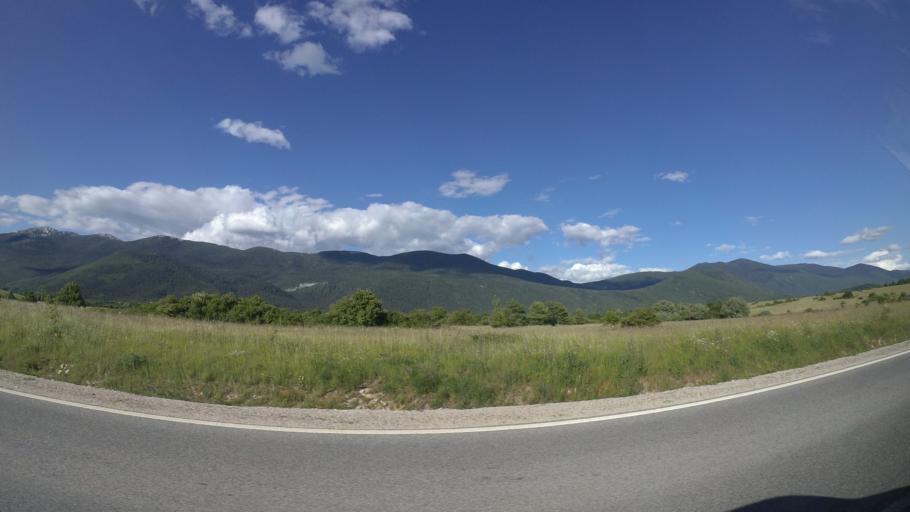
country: BA
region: Federation of Bosnia and Herzegovina
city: Izacic
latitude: 44.7308
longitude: 15.7303
